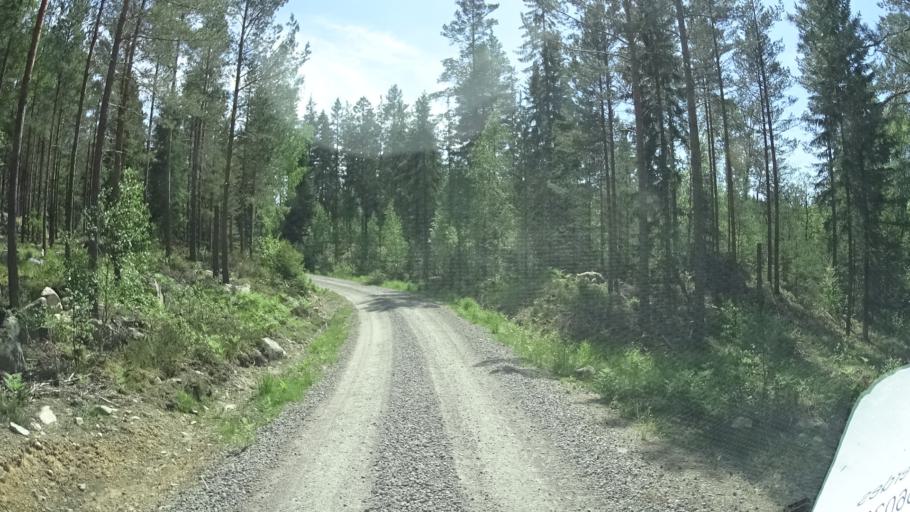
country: SE
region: OEstergoetland
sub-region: Norrkopings Kommun
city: Svartinge
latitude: 58.7824
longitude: 15.9118
